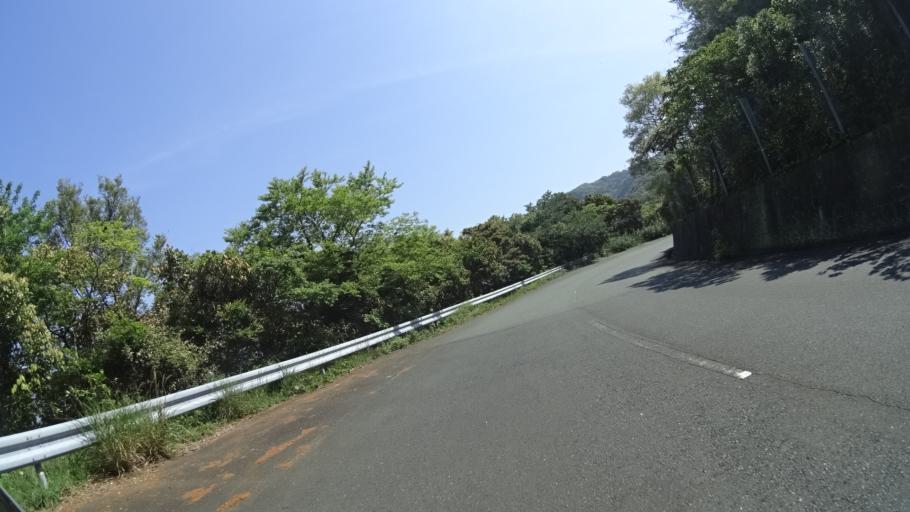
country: JP
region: Oita
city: Tsukumiura
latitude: 33.3578
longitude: 132.0333
